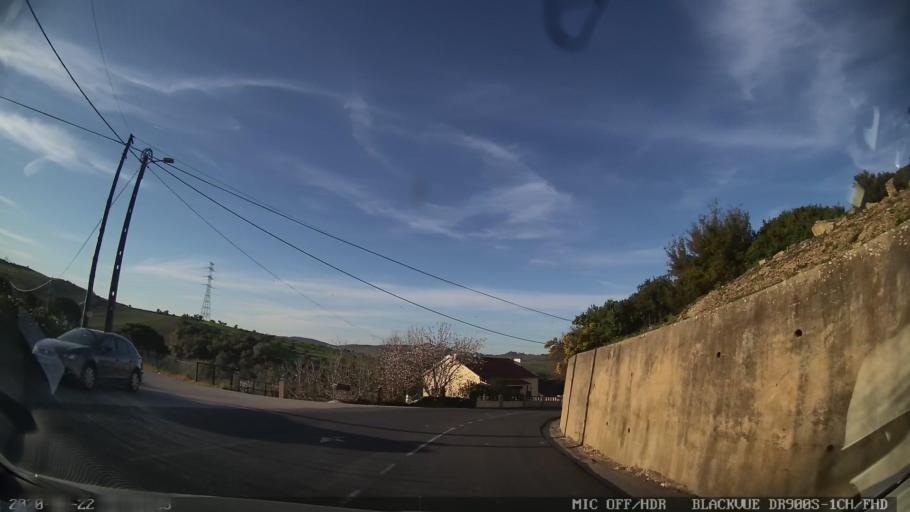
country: PT
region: Lisbon
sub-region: Vila Franca de Xira
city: Castanheira do Ribatejo
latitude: 38.9904
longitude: -9.0172
